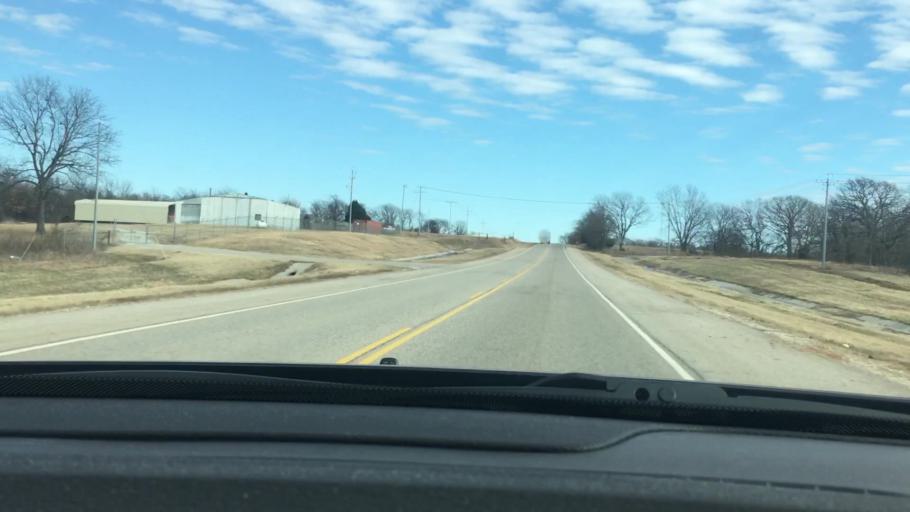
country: US
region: Oklahoma
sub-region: Garvin County
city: Stratford
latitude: 34.7967
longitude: -96.8576
